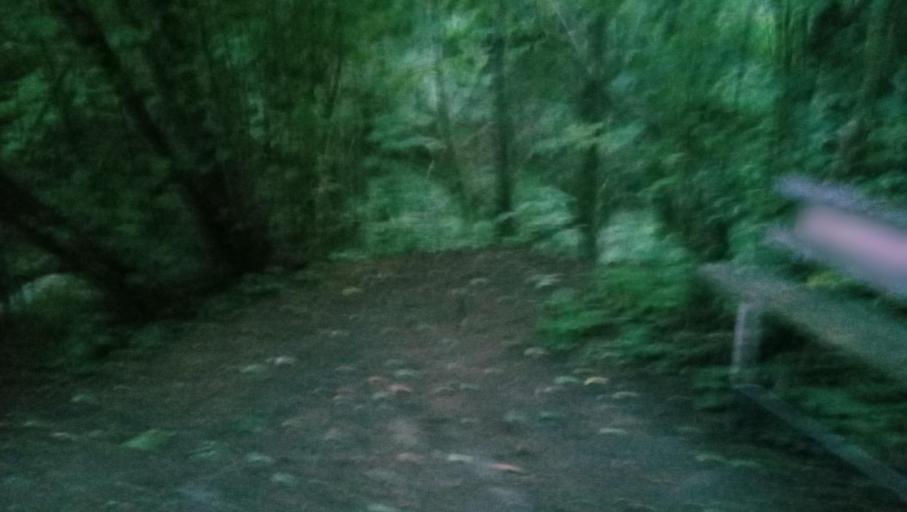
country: BY
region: Minsk
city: Dzyarzhynsk
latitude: 53.7976
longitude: 27.1676
